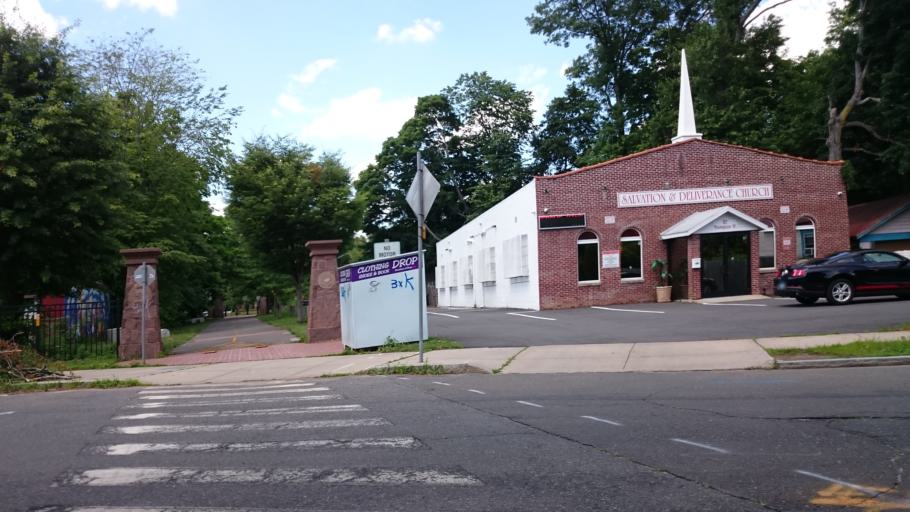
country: US
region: Connecticut
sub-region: New Haven County
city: New Haven
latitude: 41.3274
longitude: -72.9322
